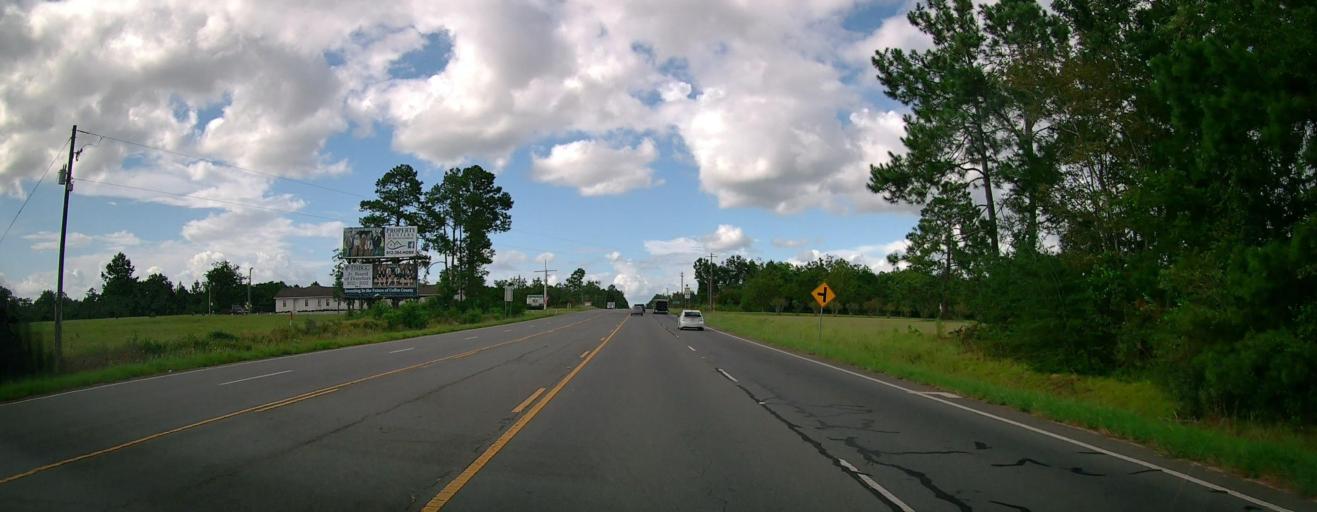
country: US
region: Georgia
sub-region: Coffee County
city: Douglas
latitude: 31.5425
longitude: -82.8510
